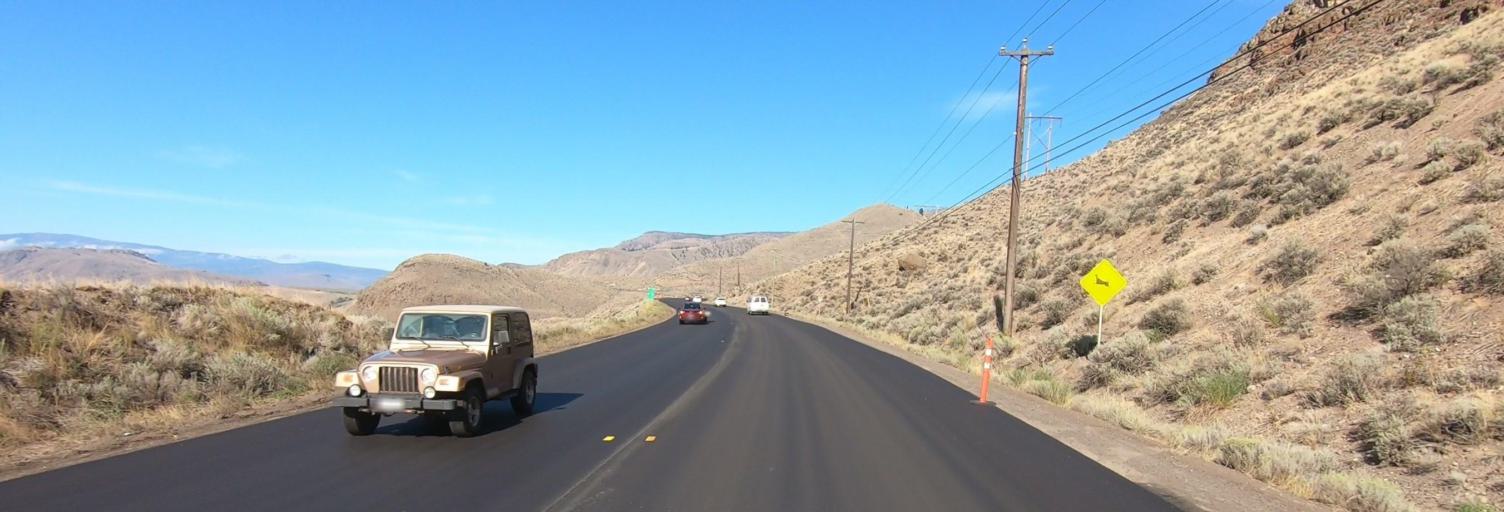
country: CA
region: British Columbia
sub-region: Thompson-Nicola Regional District
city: Ashcroft
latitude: 50.7952
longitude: -121.0935
